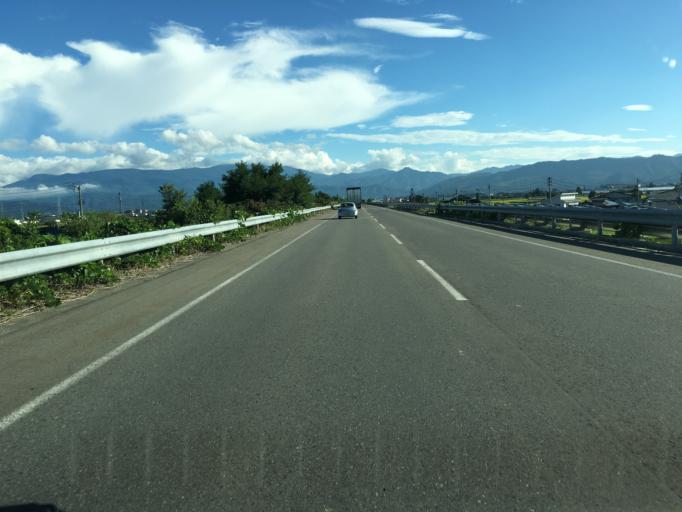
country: JP
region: Yamagata
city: Yonezawa
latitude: 37.9464
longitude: 140.1119
